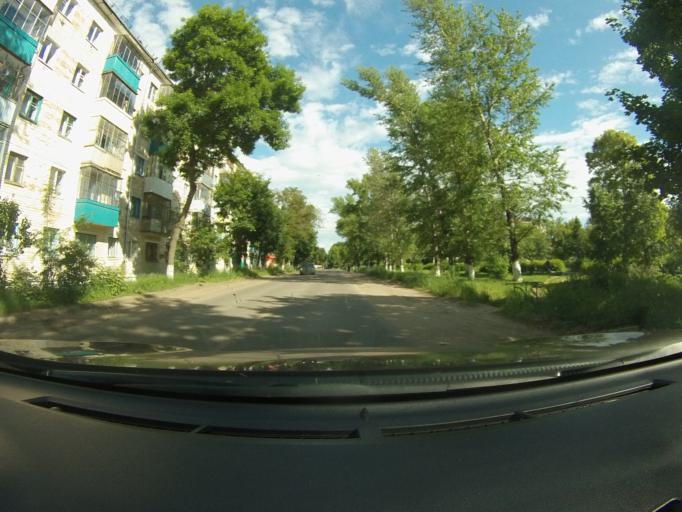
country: RU
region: Orjol
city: Mtsensk
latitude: 53.2758
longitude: 36.5729
